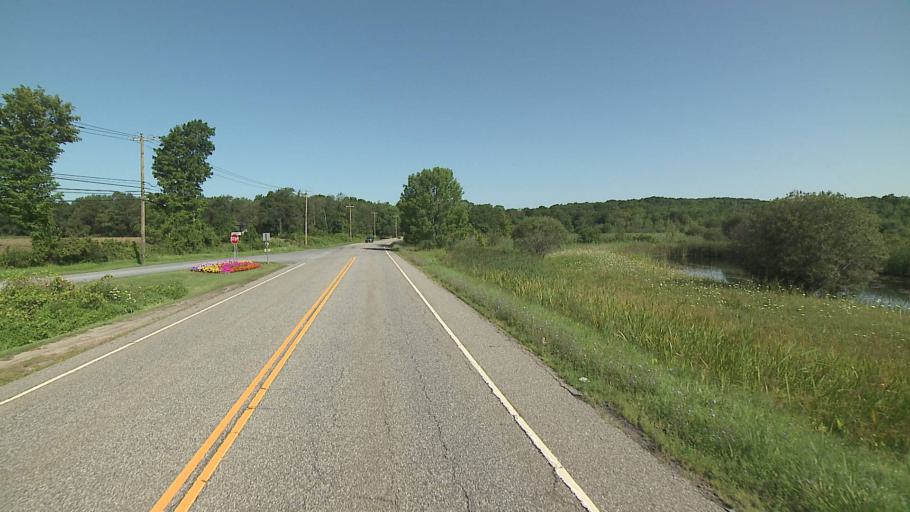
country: US
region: Connecticut
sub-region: Litchfield County
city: Kent
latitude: 41.8330
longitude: -73.4284
